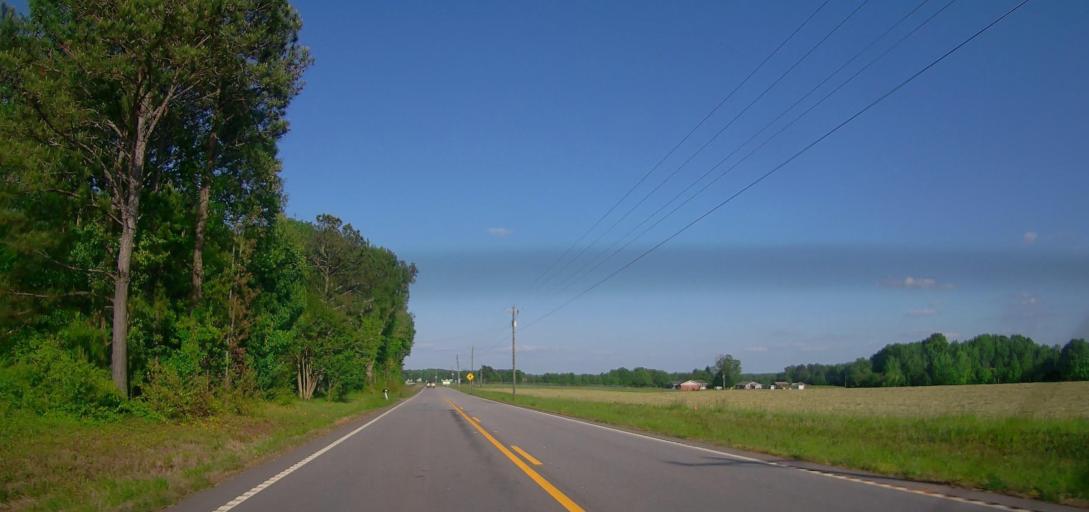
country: US
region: Georgia
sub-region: Walton County
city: Social Circle
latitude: 33.6266
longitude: -83.6607
